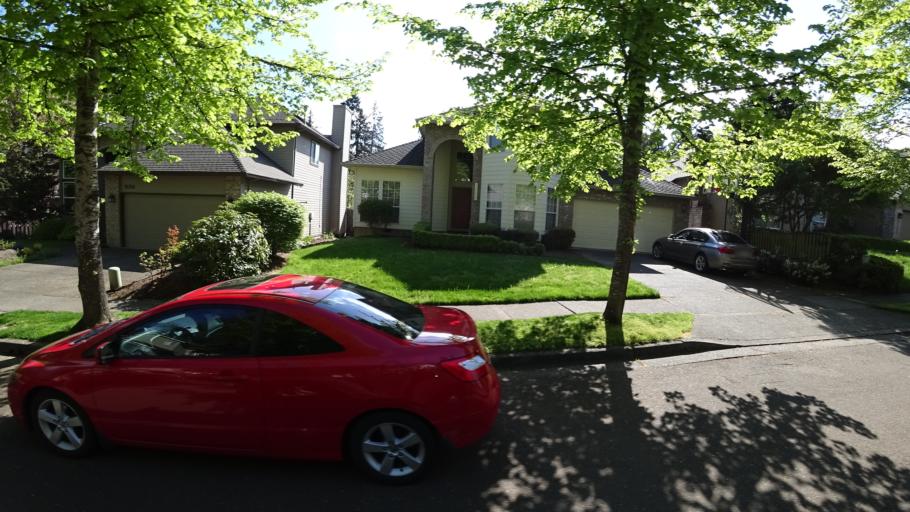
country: US
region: Oregon
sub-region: Washington County
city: King City
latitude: 45.4449
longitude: -122.8327
